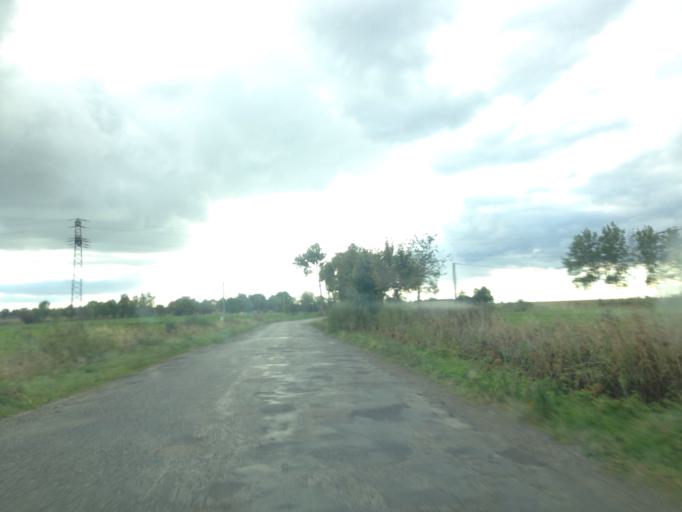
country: PL
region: Pomeranian Voivodeship
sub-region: Powiat kwidzynski
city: Prabuty
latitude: 53.7698
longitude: 19.2223
